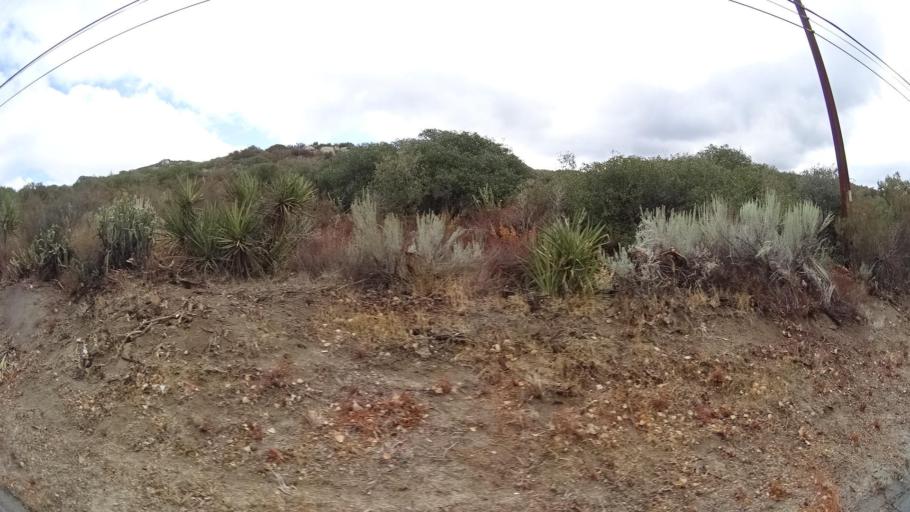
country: US
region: California
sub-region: San Diego County
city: Campo
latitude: 32.6897
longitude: -116.4322
